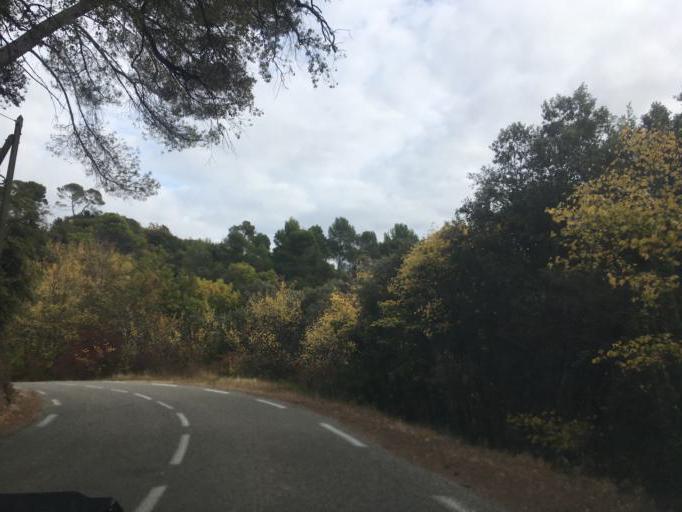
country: FR
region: Provence-Alpes-Cote d'Azur
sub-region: Departement du Var
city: Villecroze
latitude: 43.5974
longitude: 6.2836
